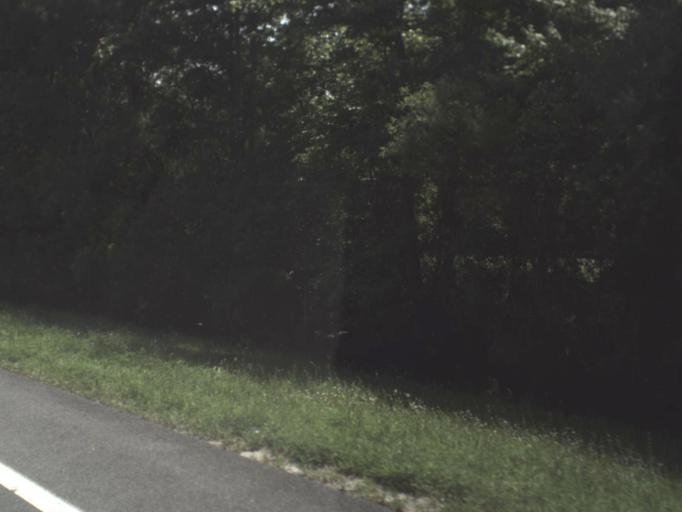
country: US
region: Florida
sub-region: Nassau County
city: Yulee
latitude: 30.4996
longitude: -81.6230
